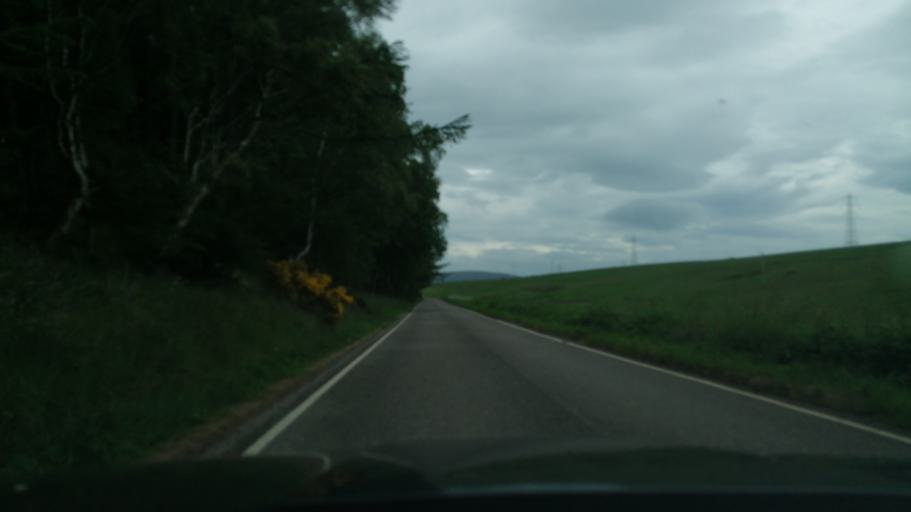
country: GB
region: Scotland
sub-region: Moray
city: Cullen
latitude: 57.5982
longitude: -2.8551
